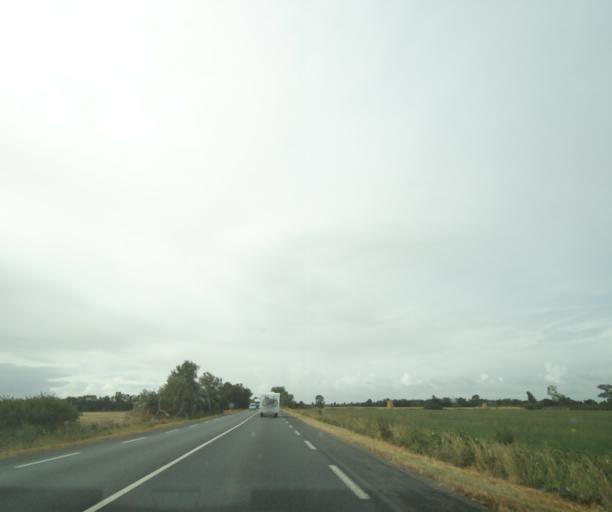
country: FR
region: Pays de la Loire
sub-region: Departement de la Vendee
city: Sainte-Gemme-la-Plaine
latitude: 46.4364
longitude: -1.0996
